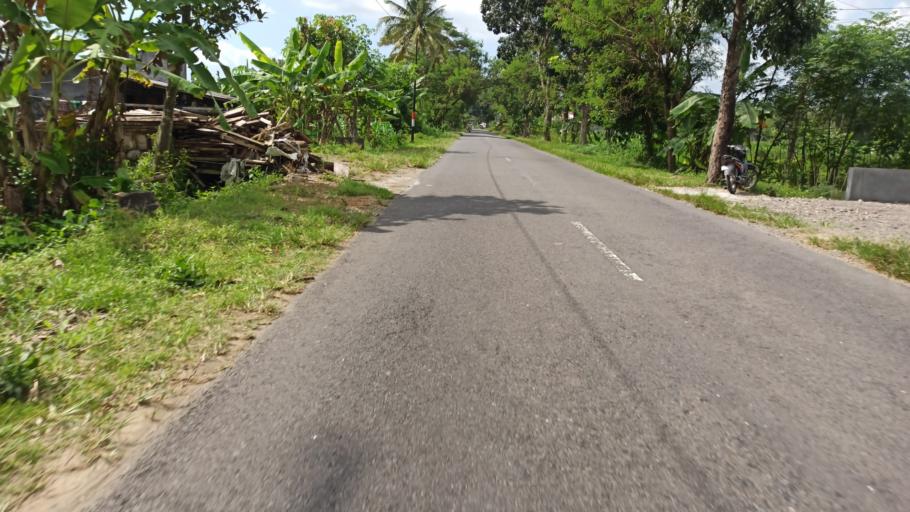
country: ID
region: Daerah Istimewa Yogyakarta
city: Sleman
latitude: -7.6895
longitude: 110.2968
